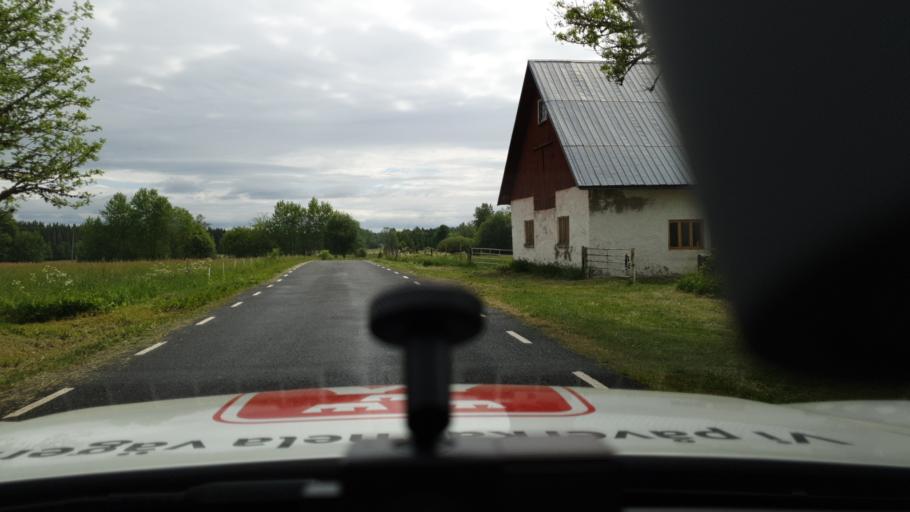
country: SE
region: Joenkoeping
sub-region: Mullsjo Kommun
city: Mullsjoe
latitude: 57.9943
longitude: 13.7343
